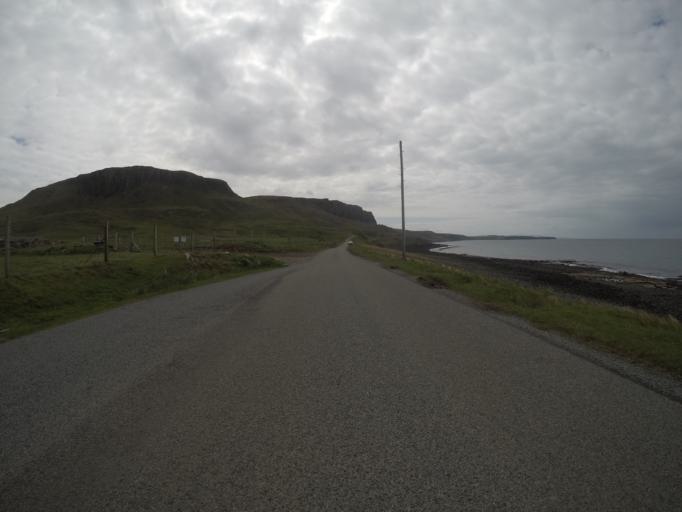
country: GB
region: Scotland
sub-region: Highland
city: Portree
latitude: 57.6793
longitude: -6.3449
